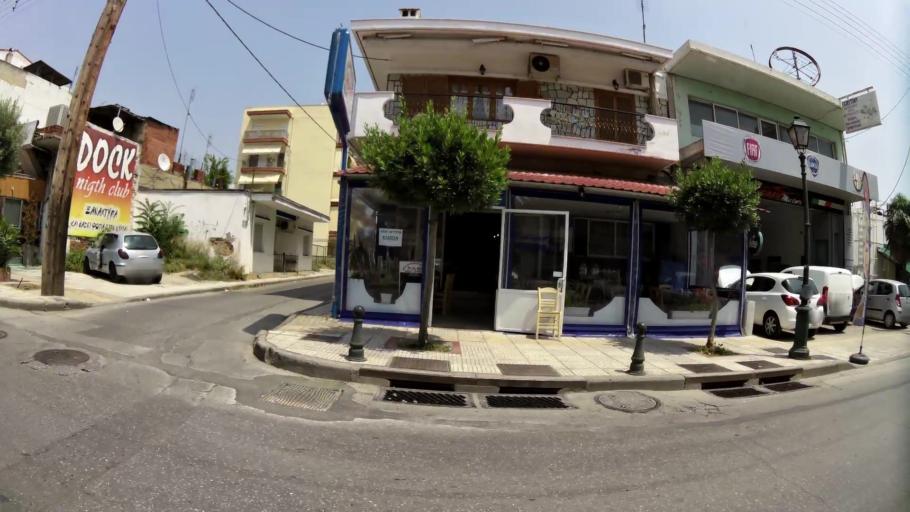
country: GR
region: Central Macedonia
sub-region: Nomos Thessalonikis
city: Evosmos
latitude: 40.6623
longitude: 22.9118
